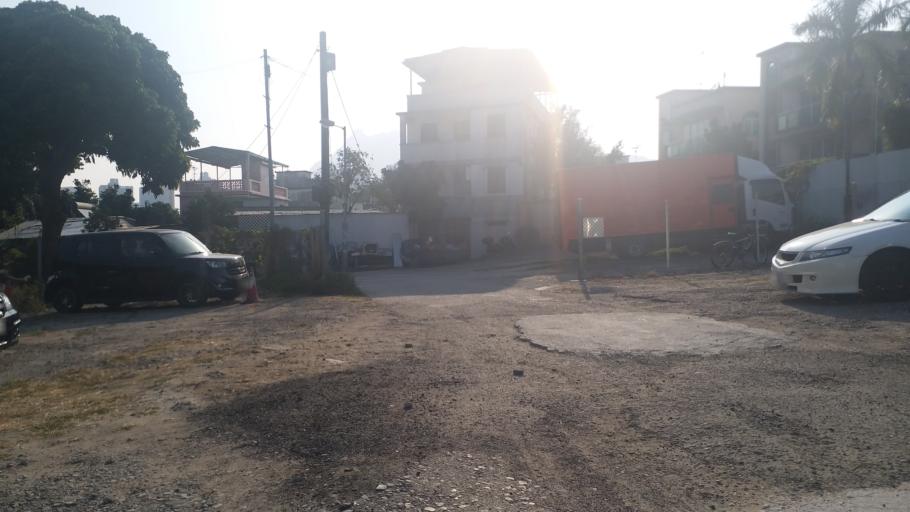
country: HK
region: Tuen Mun
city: Tuen Mun
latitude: 22.4168
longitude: 113.9753
